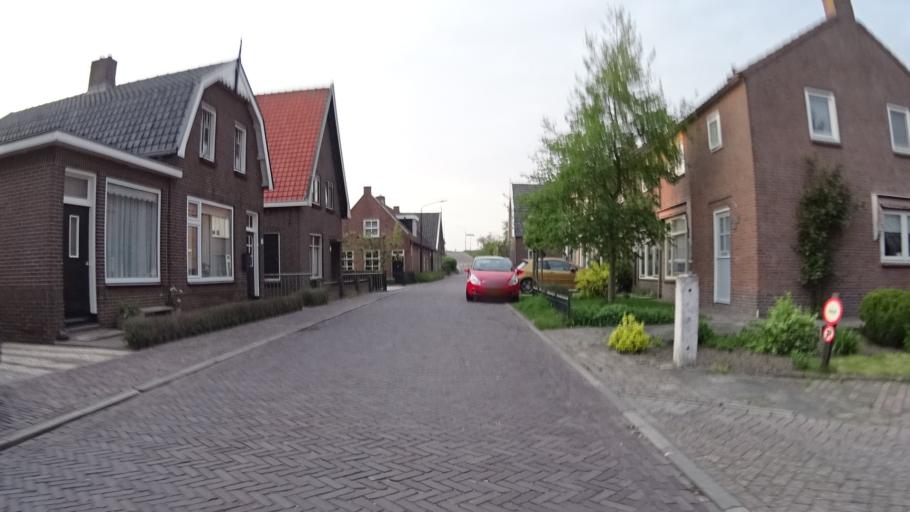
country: NL
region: North Brabant
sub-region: Gemeente Woudrichem
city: Woudrichem
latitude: 51.8148
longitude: 4.9813
